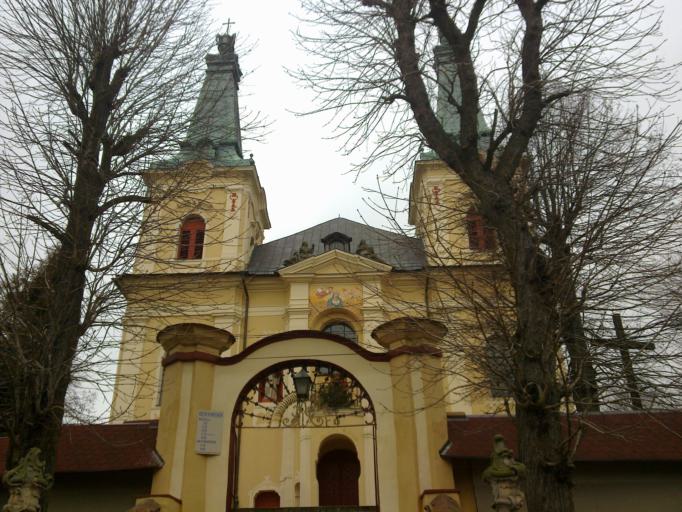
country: PL
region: Lubusz
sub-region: Powiat miedzyrzecki
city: Przytoczna
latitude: 52.5488
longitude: 15.6420
